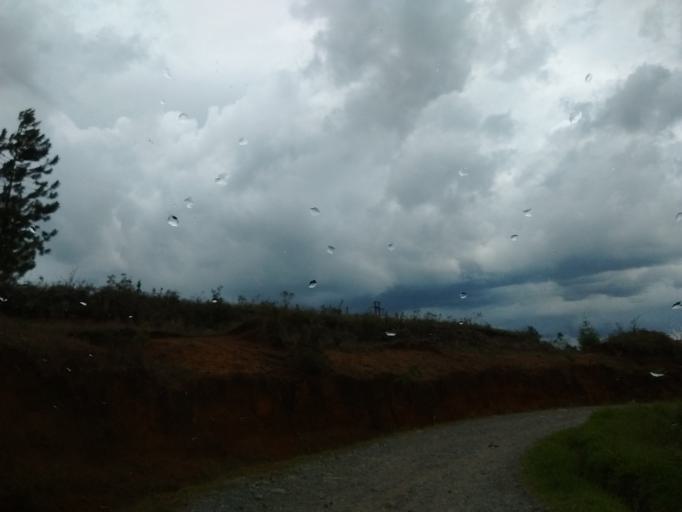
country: CO
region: Cauca
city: Cajibio
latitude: 2.5786
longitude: -76.6607
